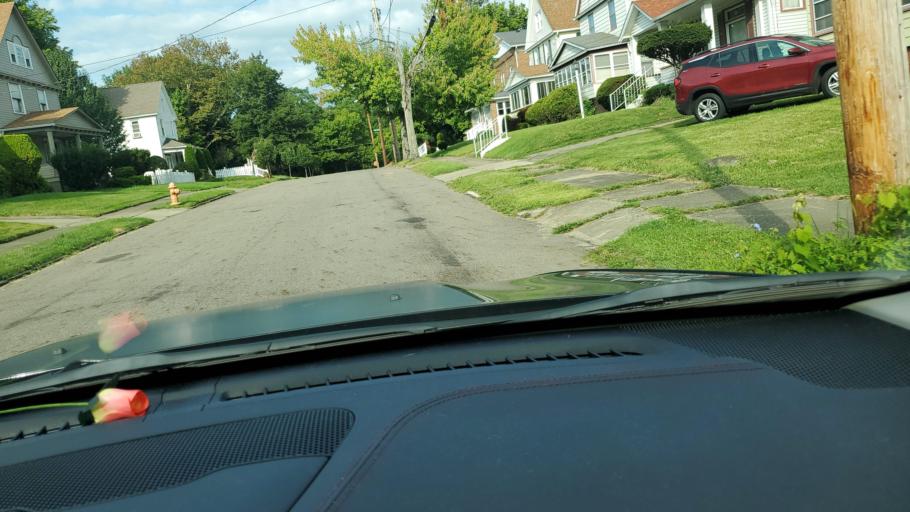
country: US
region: Ohio
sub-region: Mahoning County
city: Youngstown
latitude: 41.0954
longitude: -80.6696
